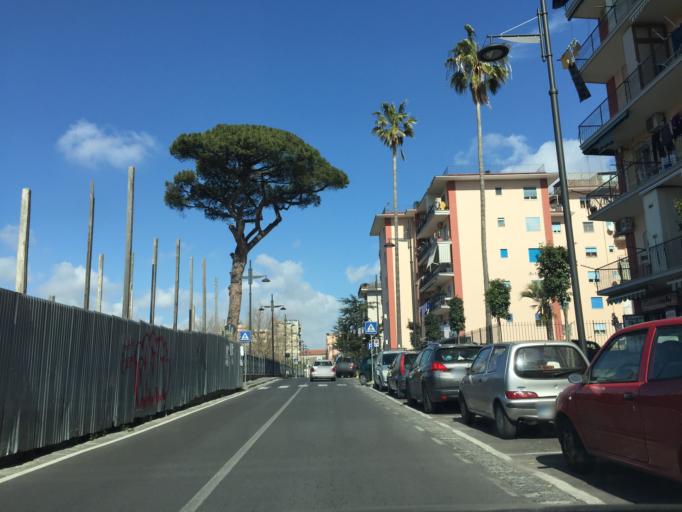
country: IT
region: Campania
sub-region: Provincia di Napoli
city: San Giorgio a Cremano
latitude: 40.8259
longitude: 14.3403
